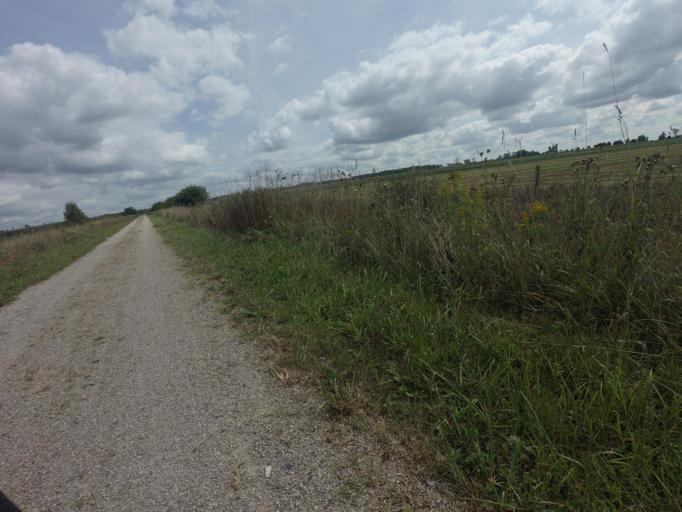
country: CA
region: Ontario
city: North Perth
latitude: 43.5666
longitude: -80.9465
